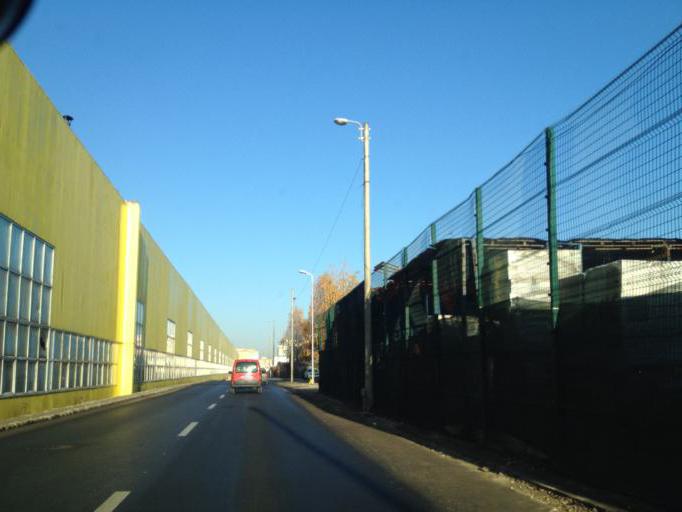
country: RO
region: Brasov
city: Brasov
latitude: 45.6298
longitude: 25.6368
